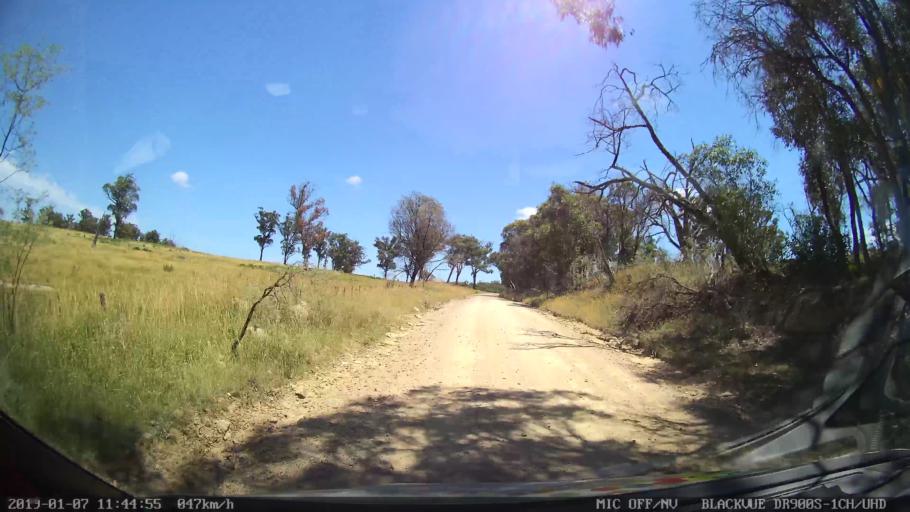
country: AU
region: New South Wales
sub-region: Guyra
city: Guyra
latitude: -30.3495
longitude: 151.6058
